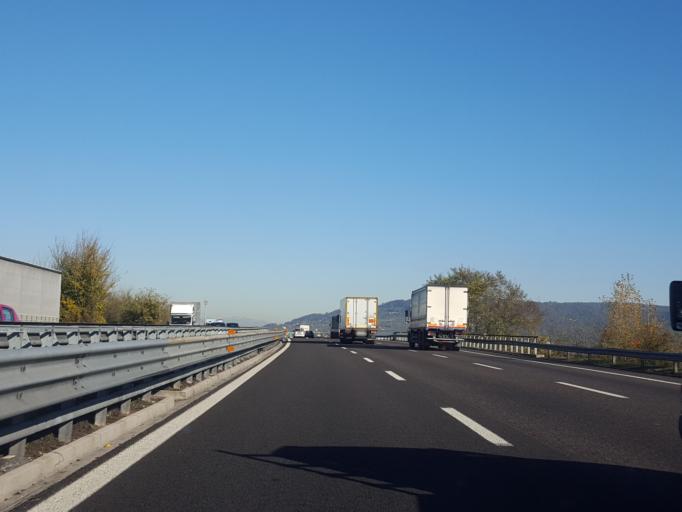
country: IT
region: Veneto
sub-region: Provincia di Vicenza
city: Montebello Vicentino
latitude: 45.4574
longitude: 11.3995
